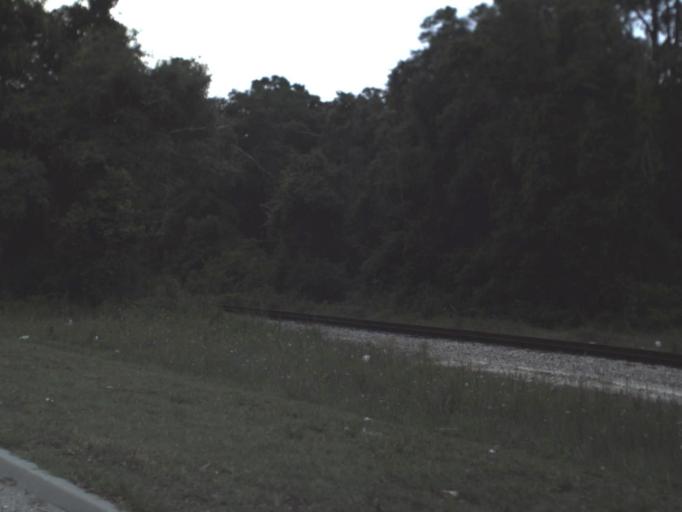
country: US
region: Florida
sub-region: Duval County
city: Jacksonville
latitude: 30.4111
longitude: -81.5671
